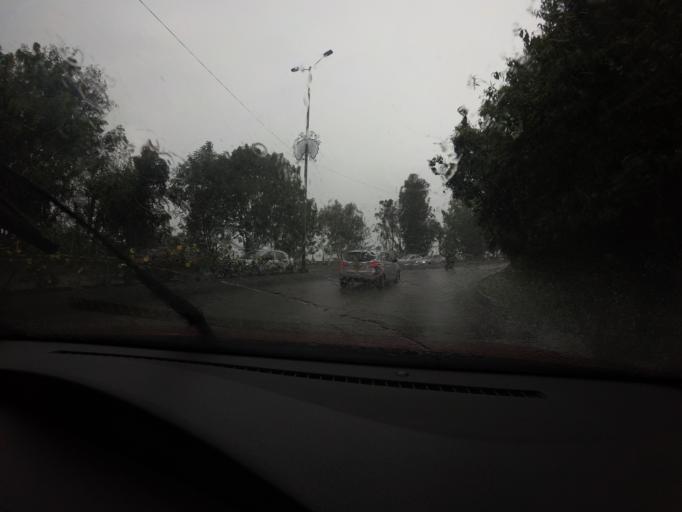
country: CO
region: Caldas
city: Villamaria
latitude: 5.0421
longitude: -75.4803
